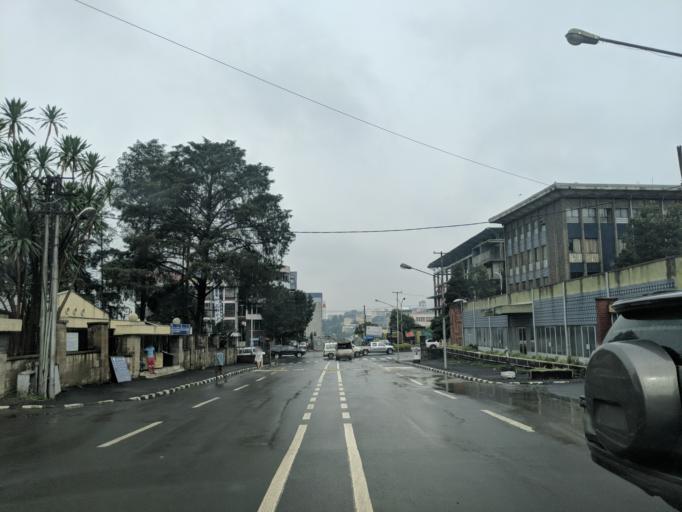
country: ET
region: Adis Abeba
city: Addis Ababa
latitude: 9.0308
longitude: 38.7643
